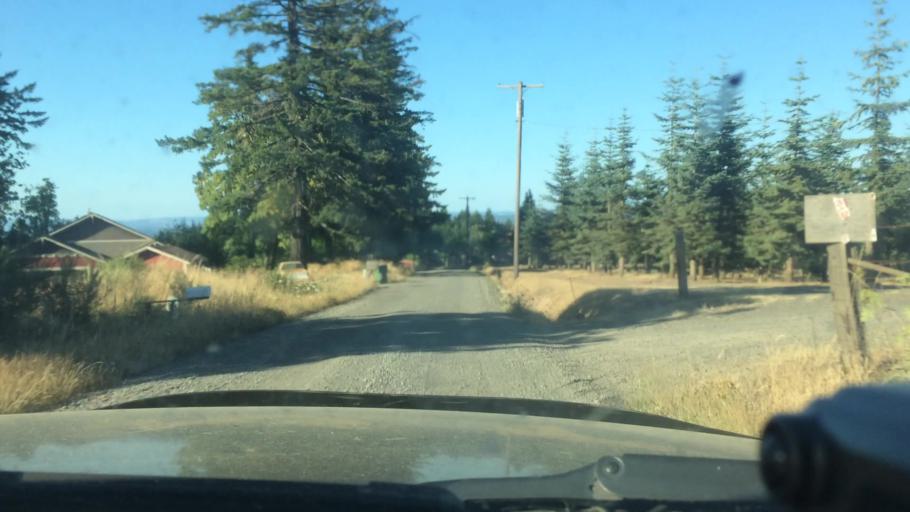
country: US
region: Oregon
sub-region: Yamhill County
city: Newberg
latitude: 45.3674
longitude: -122.9807
